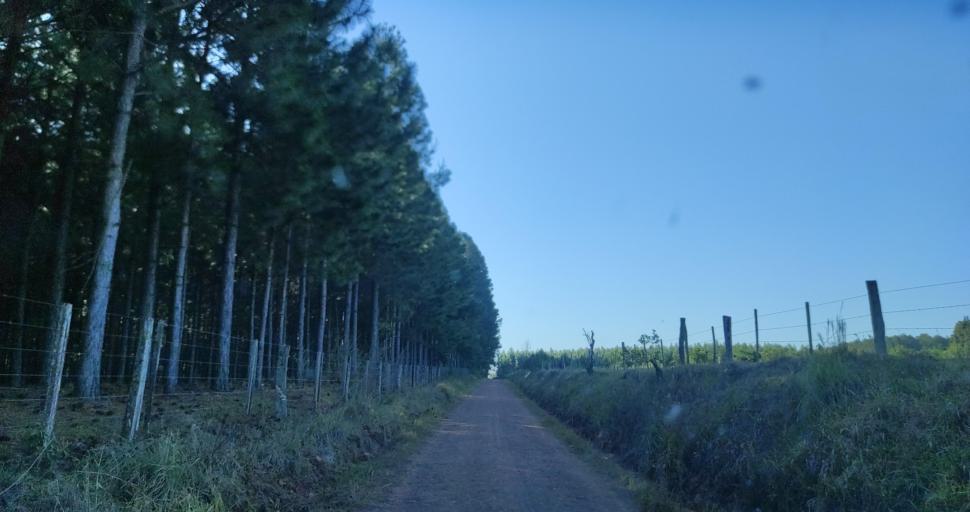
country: AR
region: Misiones
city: Capiovi
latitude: -26.8910
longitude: -55.1073
